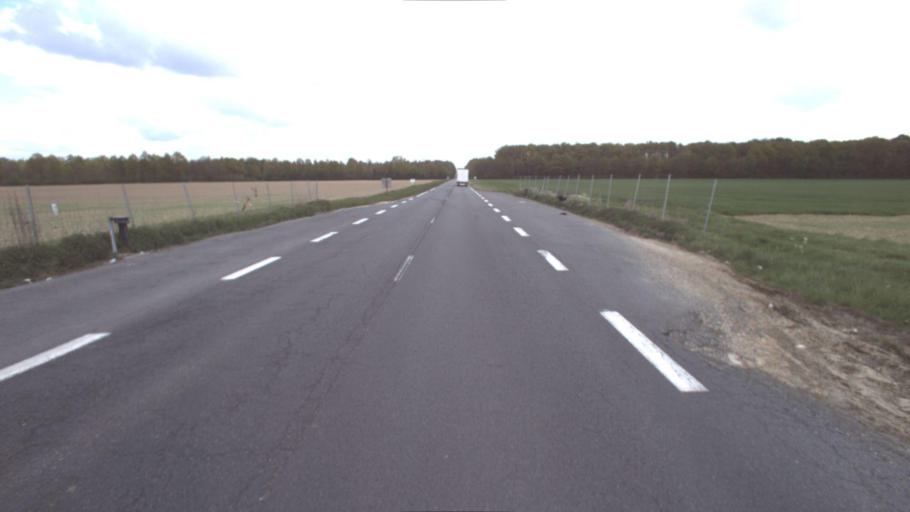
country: FR
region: Ile-de-France
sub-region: Departement de Seine-et-Marne
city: Villiers-Saint-Georges
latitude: 48.7026
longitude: 3.4572
